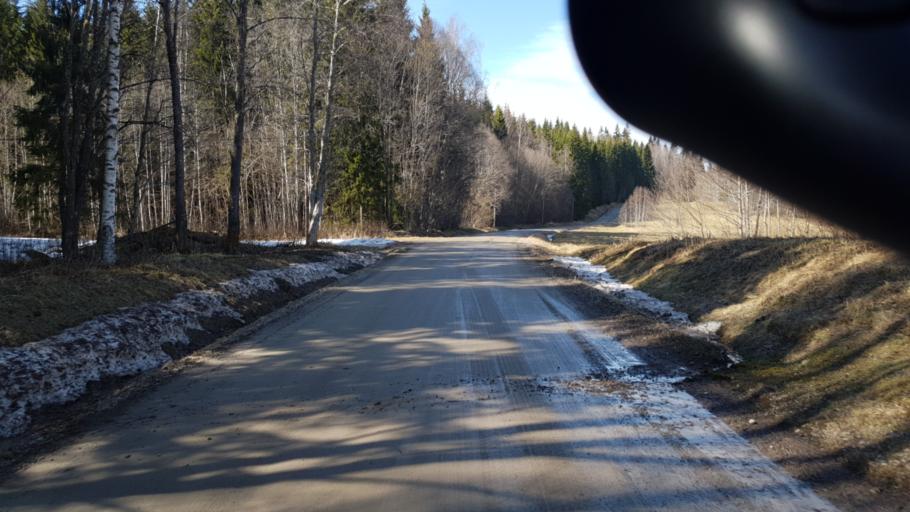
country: SE
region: Vaermland
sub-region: Sunne Kommun
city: Sunne
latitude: 59.6938
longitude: 12.8873
